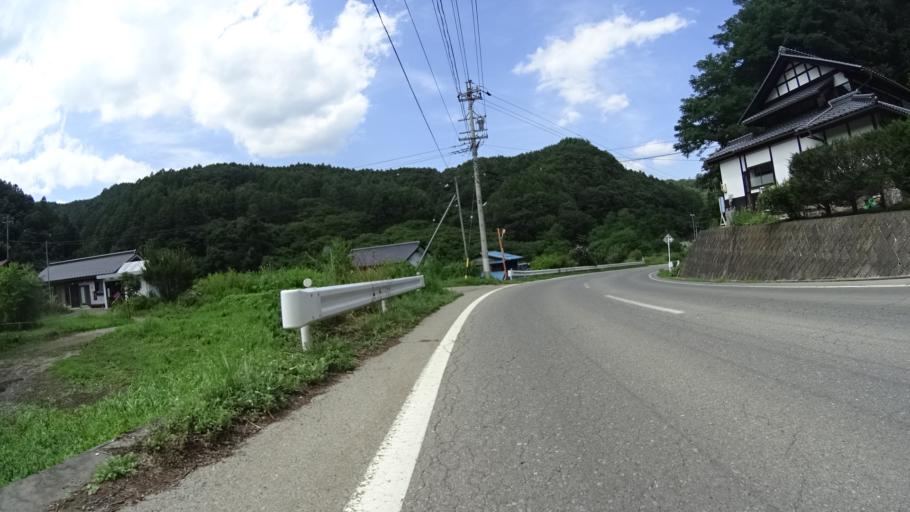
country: JP
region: Nagano
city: Saku
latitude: 36.0608
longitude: 138.5030
